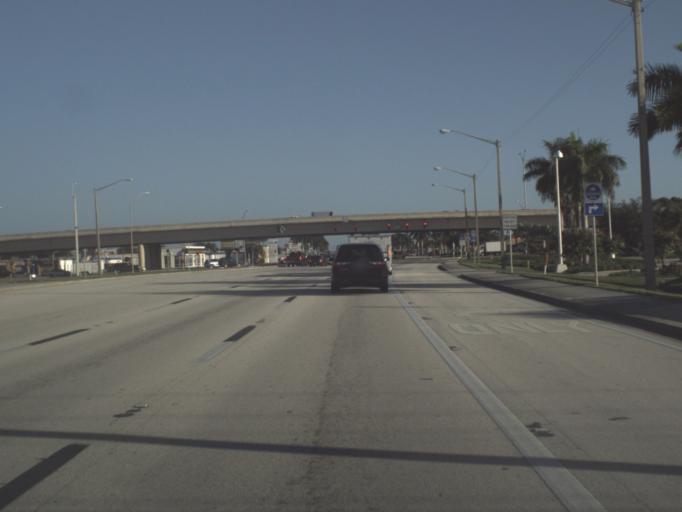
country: US
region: Florida
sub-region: Lee County
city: Pine Manor
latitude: 26.5951
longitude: -81.8718
